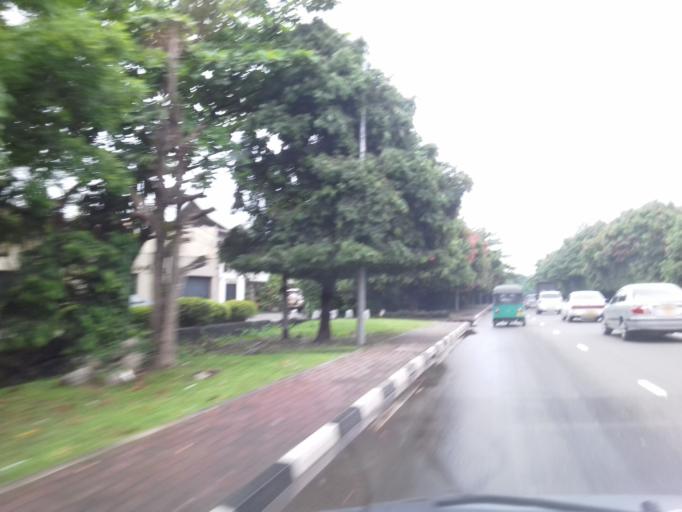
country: LK
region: Western
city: Battaramulla South
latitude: 6.8980
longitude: 79.9138
